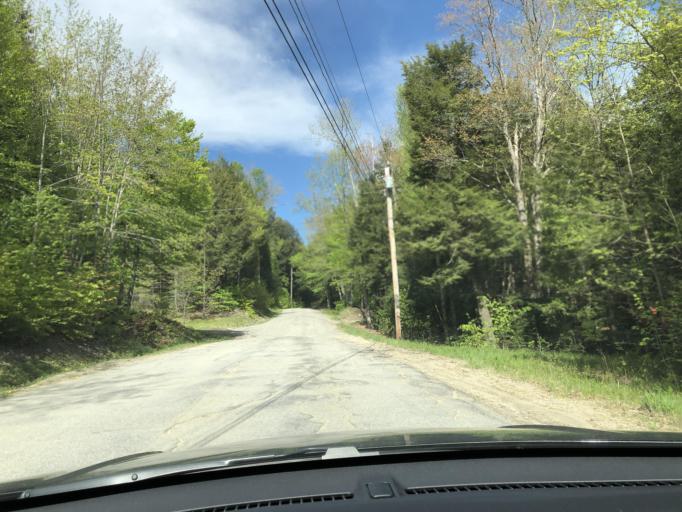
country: US
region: New Hampshire
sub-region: Merrimack County
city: New London
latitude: 43.4103
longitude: -72.0233
